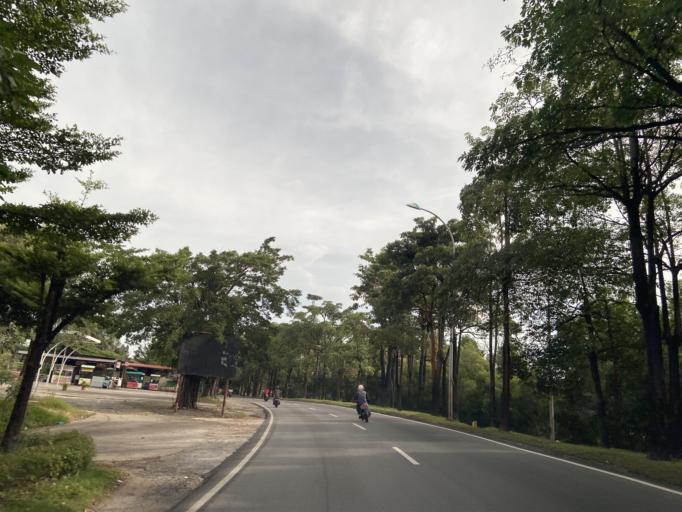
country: SG
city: Singapore
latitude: 1.1428
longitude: 104.0229
